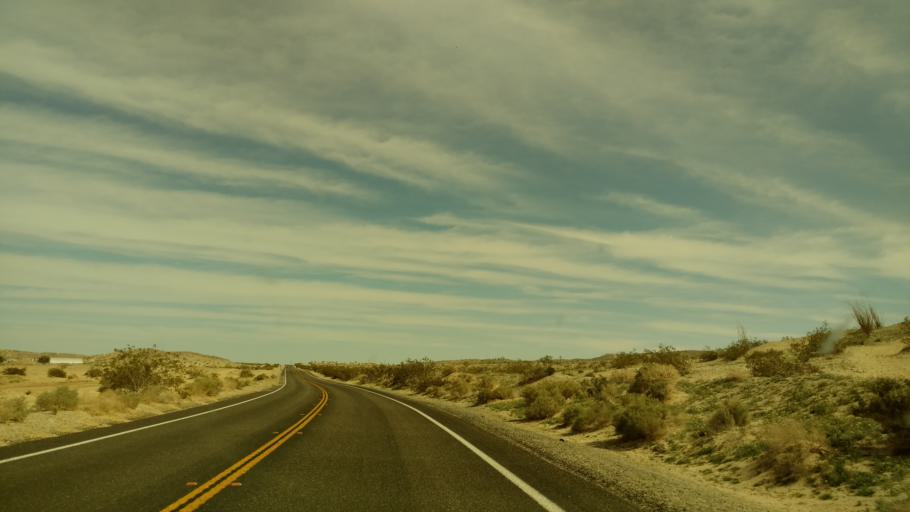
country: US
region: California
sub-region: Imperial County
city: Salton City
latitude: 33.1432
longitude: -116.1290
